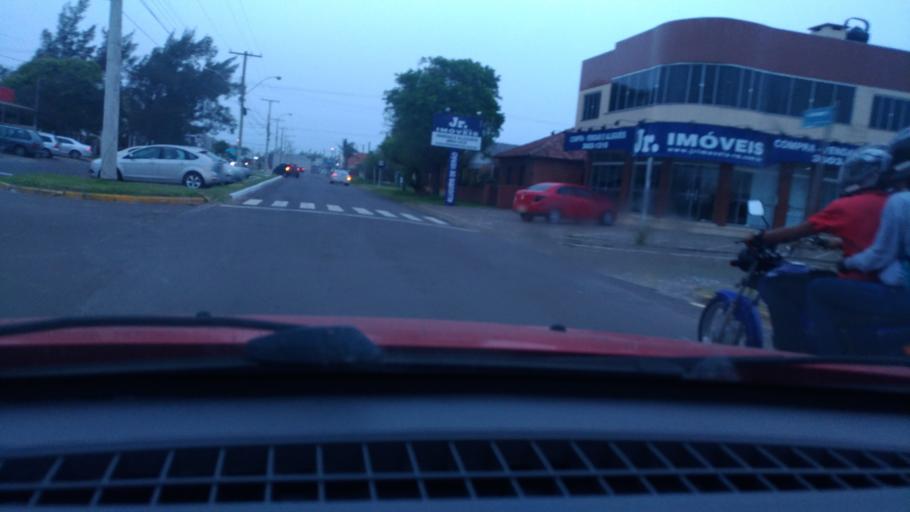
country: BR
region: Rio Grande do Sul
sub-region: Capao Da Canoa
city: Capao da Canoa
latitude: -29.8519
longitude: -50.0694
